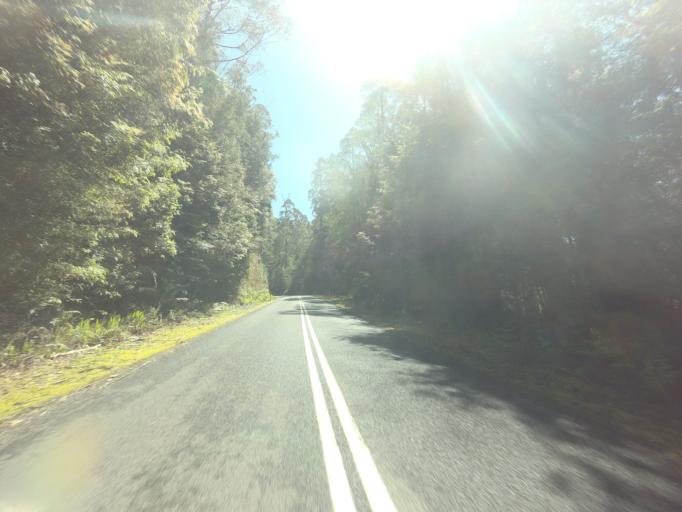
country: AU
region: Tasmania
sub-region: Huon Valley
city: Geeveston
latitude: -42.8201
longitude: 146.3090
